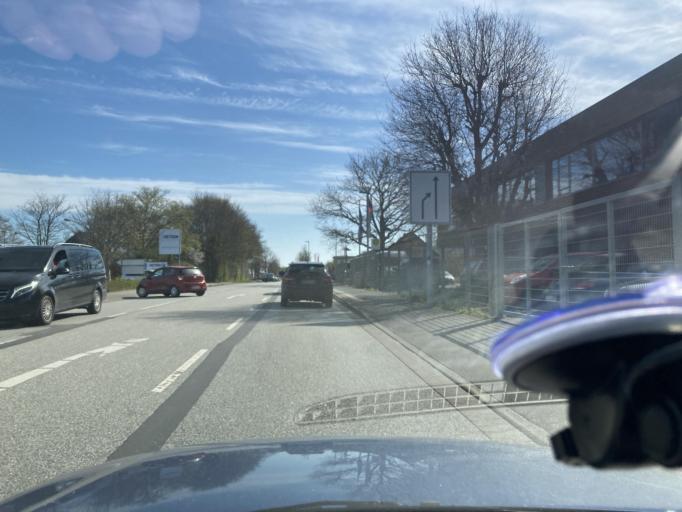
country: DE
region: Schleswig-Holstein
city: Heide
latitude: 54.1965
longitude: 9.1257
